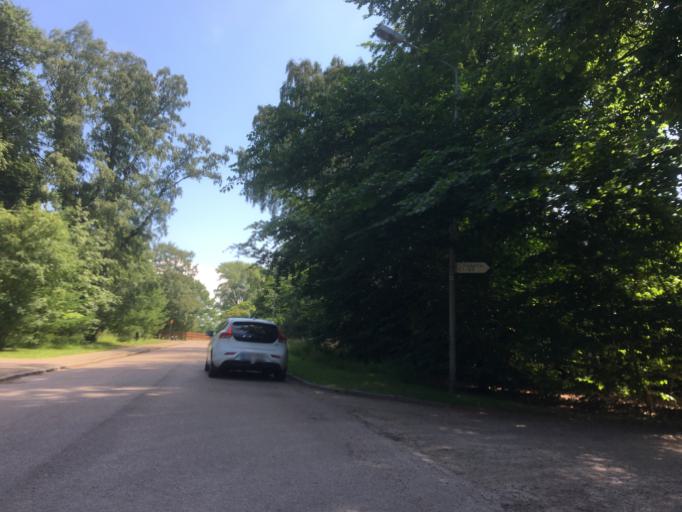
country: SE
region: Skane
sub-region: Landskrona
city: Landskrona
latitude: 55.8772
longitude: 12.8209
